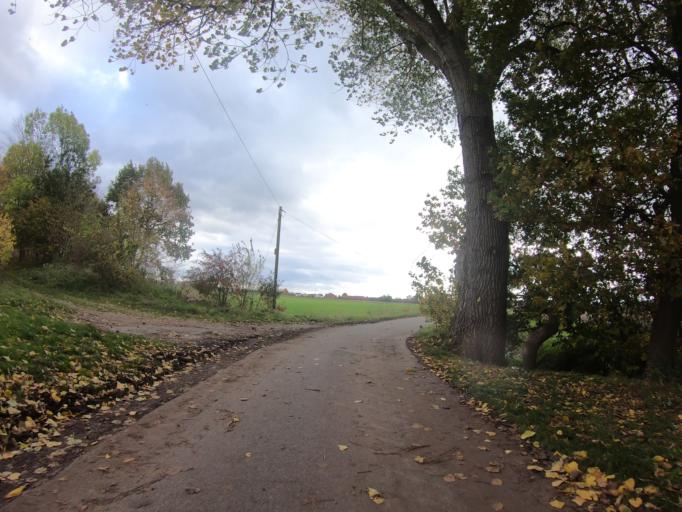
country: DE
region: Lower Saxony
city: Adenbuettel
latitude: 52.3846
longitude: 10.4854
